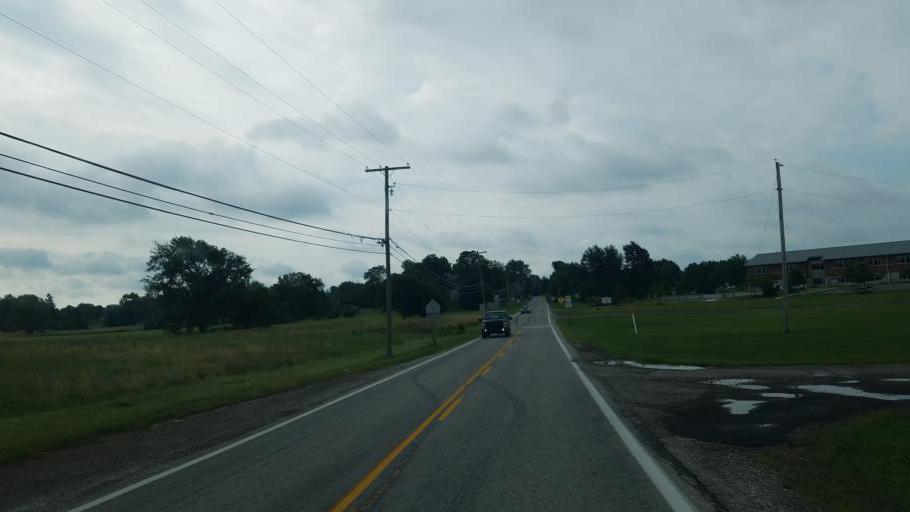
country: US
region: Ohio
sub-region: Knox County
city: Centerburg
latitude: 40.3983
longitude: -82.7041
